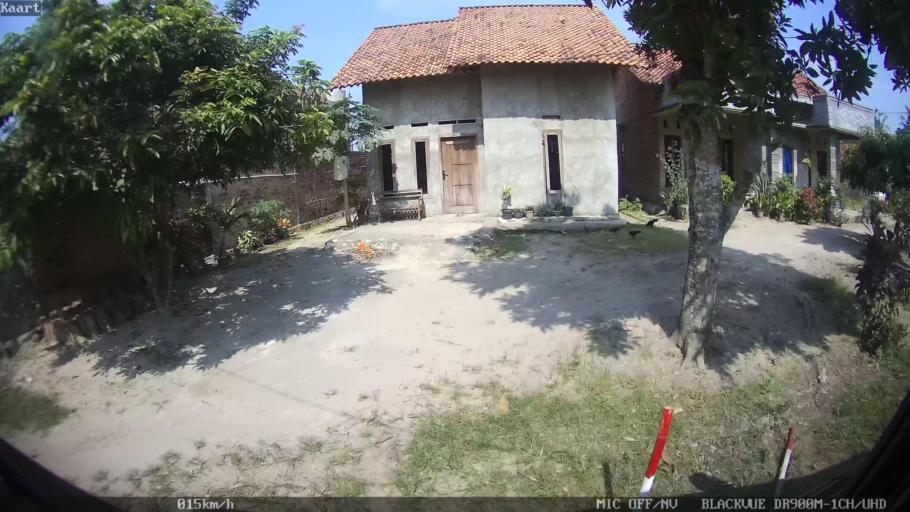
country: ID
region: Lampung
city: Natar
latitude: -5.2622
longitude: 105.2129
